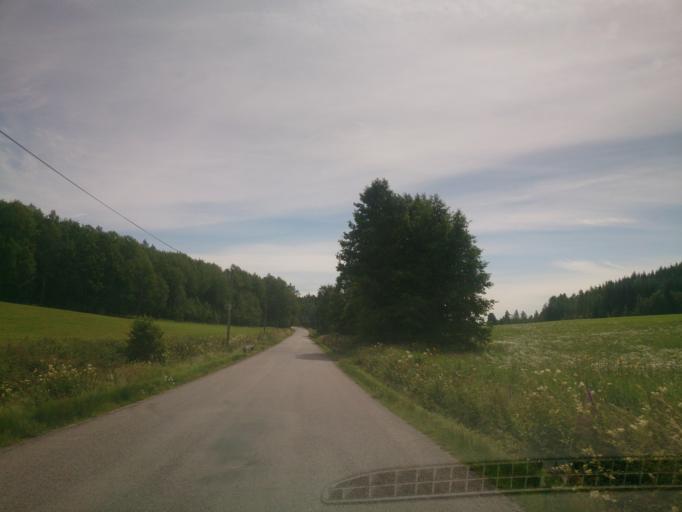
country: SE
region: OEstergoetland
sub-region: Soderkopings Kommun
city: Soederkoeping
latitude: 58.3172
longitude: 16.3077
